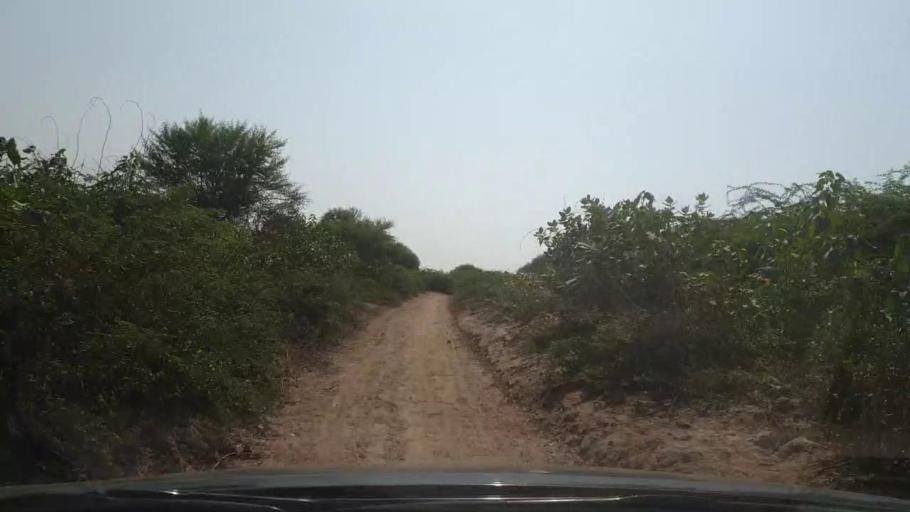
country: PK
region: Sindh
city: Naukot
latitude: 24.8099
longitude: 69.2613
